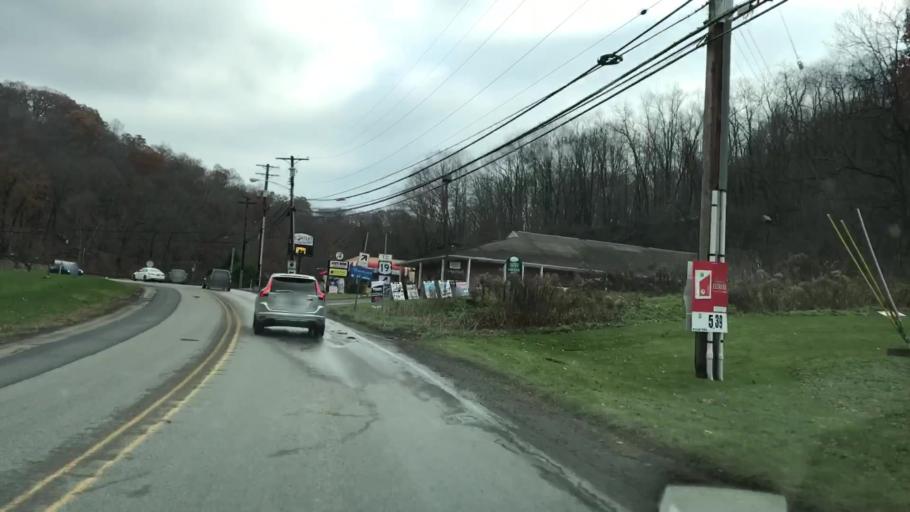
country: US
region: Pennsylvania
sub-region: Allegheny County
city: West View
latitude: 40.5342
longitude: -80.0527
